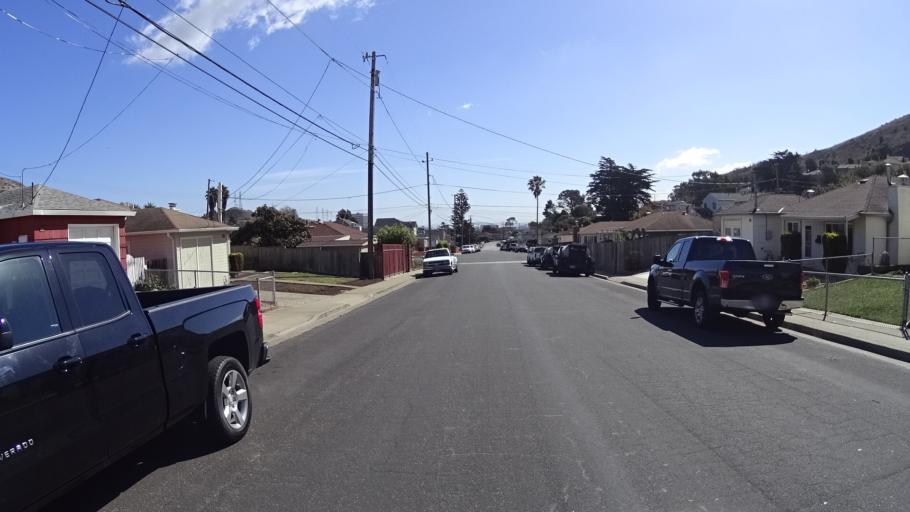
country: US
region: California
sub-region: San Mateo County
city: South San Francisco
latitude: 37.6674
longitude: -122.4148
